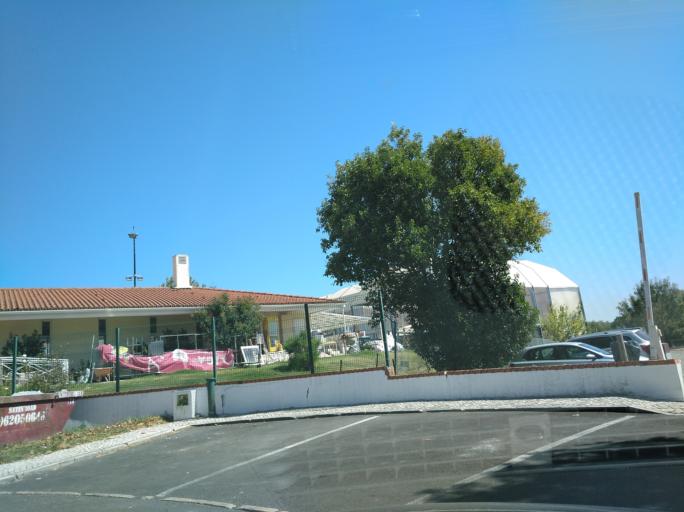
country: PT
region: Lisbon
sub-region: Loures
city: Moscavide
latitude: 38.7582
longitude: -9.1348
